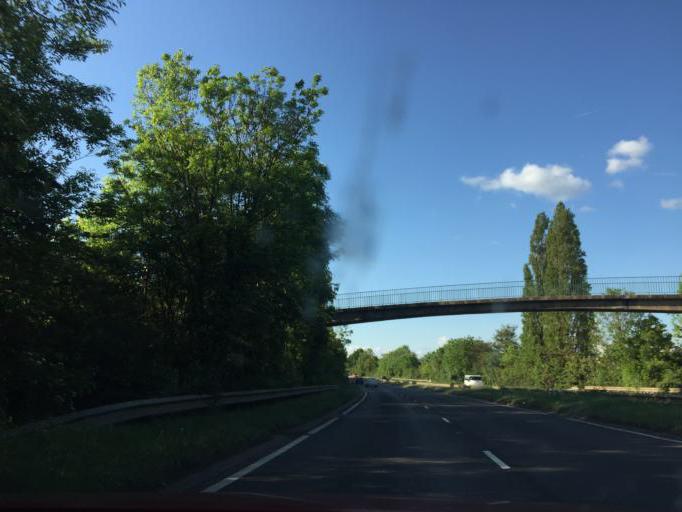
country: GB
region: England
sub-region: Warwickshire
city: Exhall
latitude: 52.4697
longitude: -1.4889
